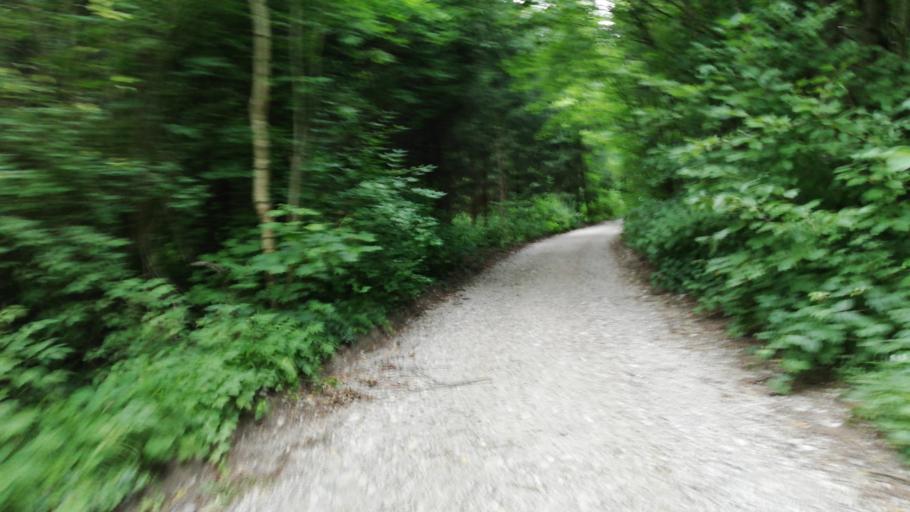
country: AT
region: Upper Austria
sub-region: Wels Stadt
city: Wels
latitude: 48.1887
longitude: 13.9968
